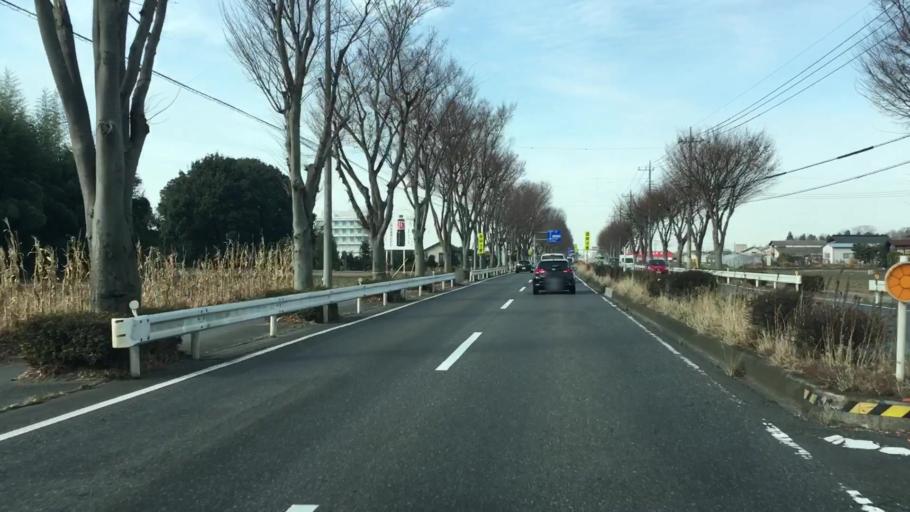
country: JP
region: Gunma
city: Tatebayashi
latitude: 36.2310
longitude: 139.5566
